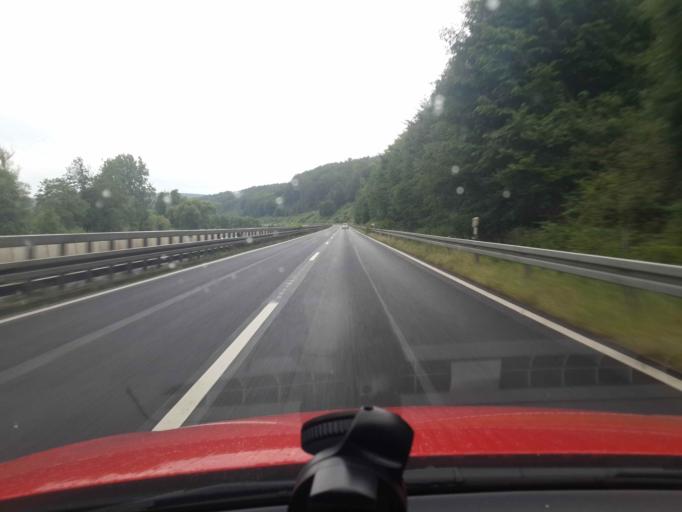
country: DE
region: Bavaria
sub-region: Regierungsbezirk Unterfranken
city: Obernburg am Main
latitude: 49.8222
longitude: 9.1363
